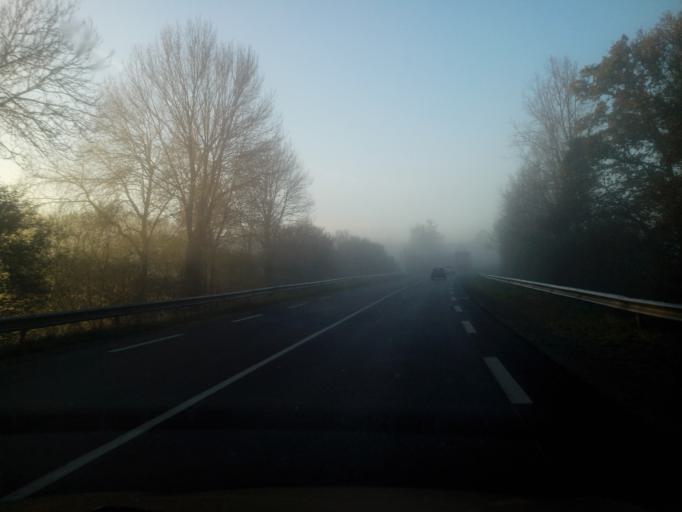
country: FR
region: Brittany
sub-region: Departement du Morbihan
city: Mauron
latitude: 48.0360
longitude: -2.3029
